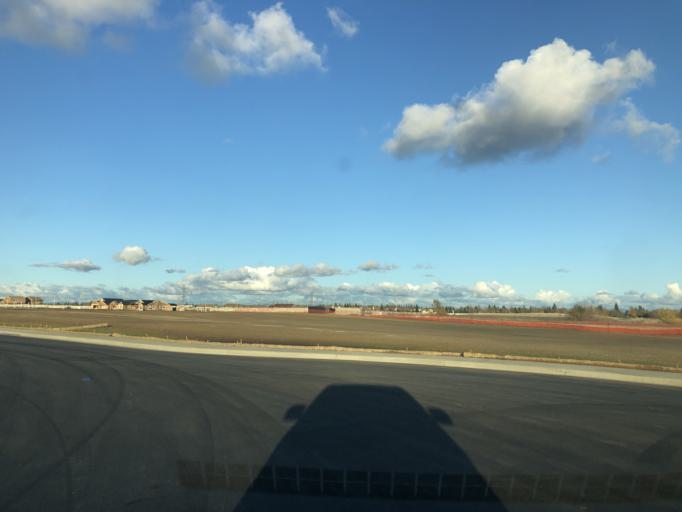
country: US
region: California
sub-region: Sacramento County
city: Antelope
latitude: 38.7561
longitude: -121.3662
